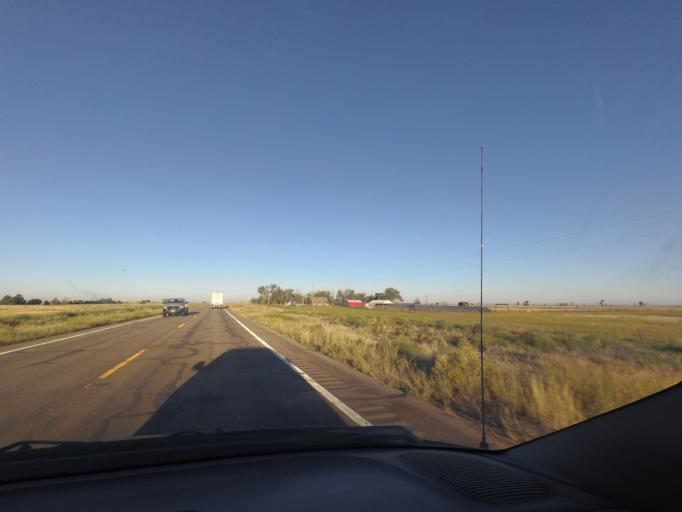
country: US
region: Colorado
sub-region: Yuma County
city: Yuma
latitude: 39.6702
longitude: -102.8840
